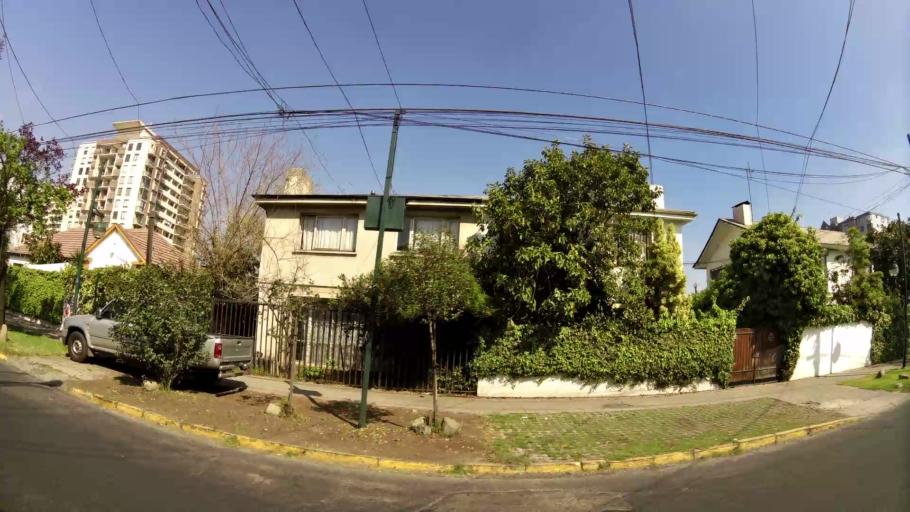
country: CL
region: Santiago Metropolitan
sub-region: Provincia de Santiago
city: Villa Presidente Frei, Nunoa, Santiago, Chile
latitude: -33.4466
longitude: -70.6125
